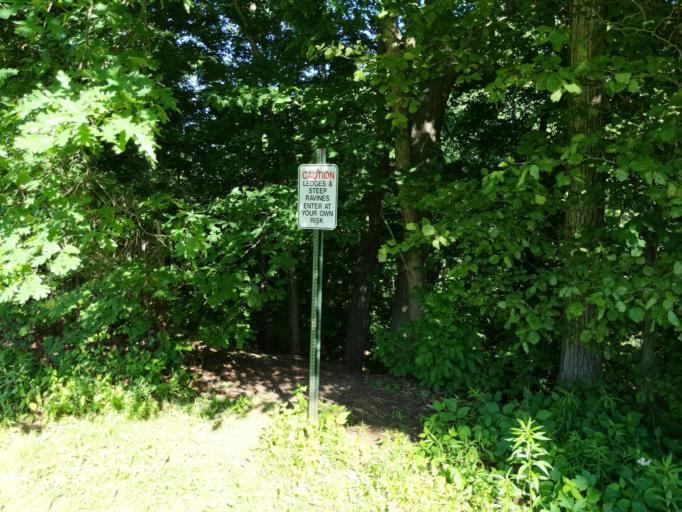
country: US
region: Michigan
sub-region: Eaton County
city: Grand Ledge
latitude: 42.7585
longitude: -84.7616
